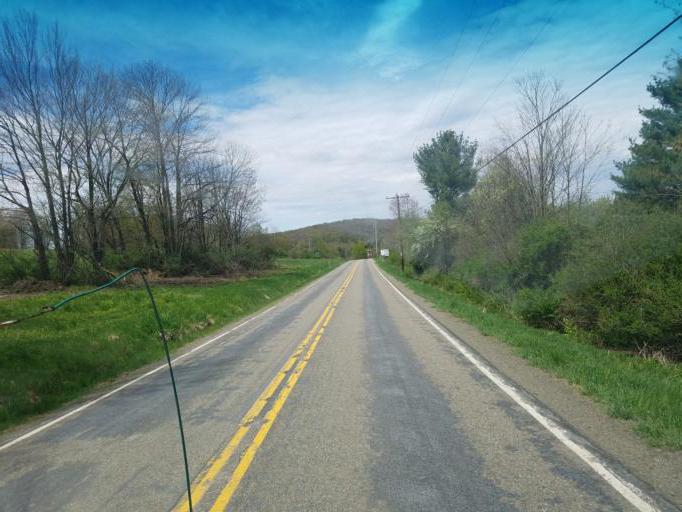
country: US
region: Pennsylvania
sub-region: Tioga County
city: Wellsboro
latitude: 41.6975
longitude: -77.4221
